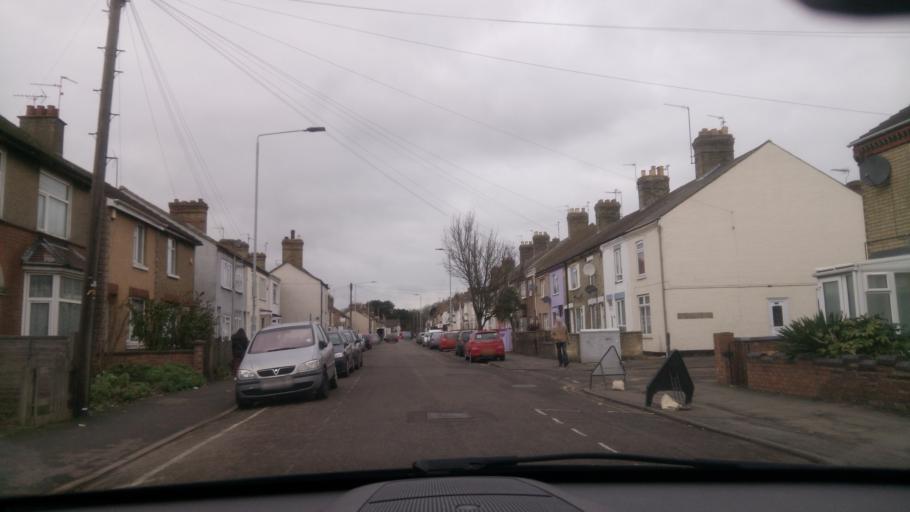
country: GB
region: England
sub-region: Peterborough
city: Peterborough
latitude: 52.5788
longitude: -0.2294
